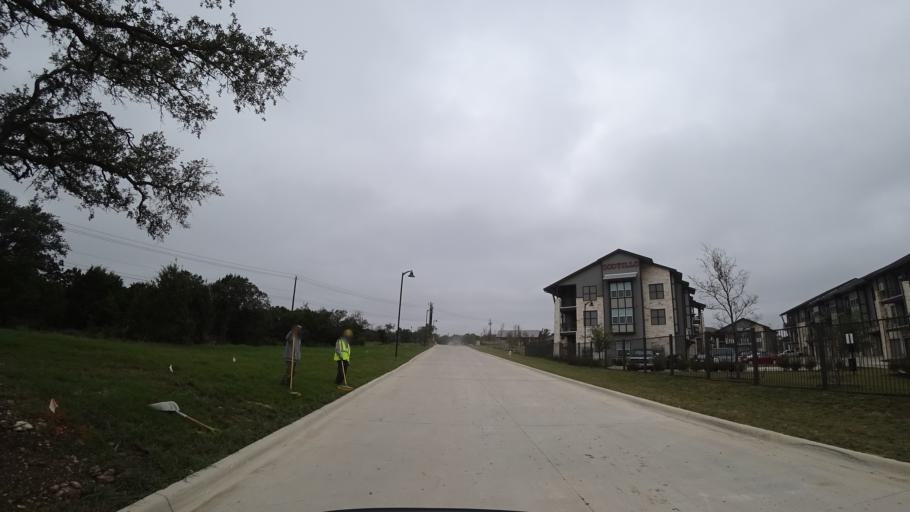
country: US
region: Texas
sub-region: Travis County
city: Barton Creek
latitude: 30.2306
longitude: -97.8882
